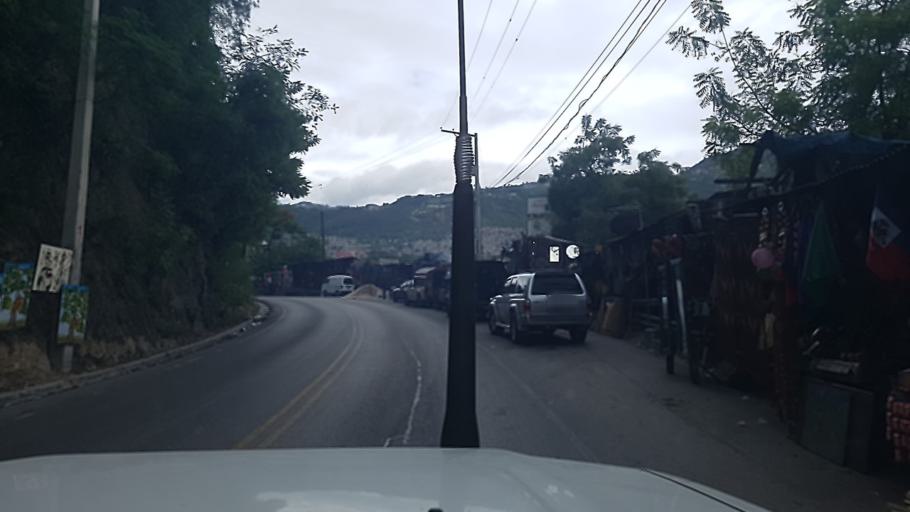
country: HT
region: Ouest
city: Delmas 73
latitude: 18.5282
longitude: -72.3004
